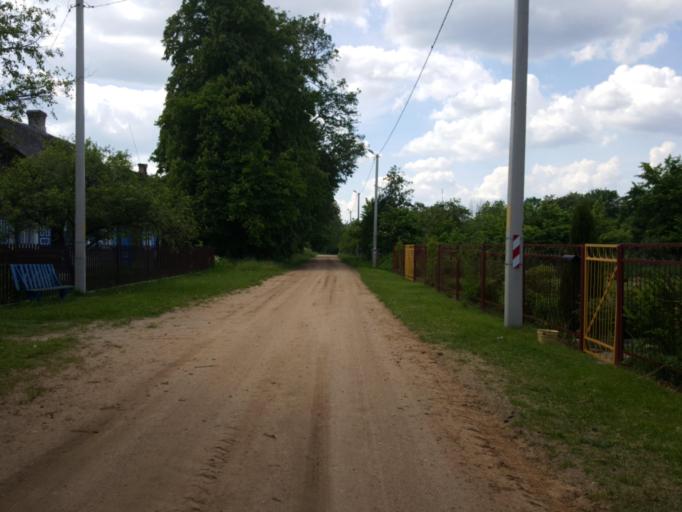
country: BY
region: Brest
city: Kamyanyuki
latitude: 52.5618
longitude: 23.6352
